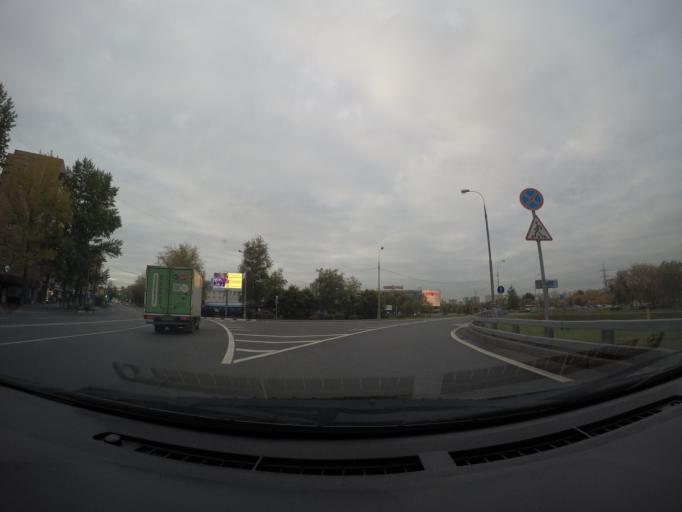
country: RU
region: Moscow
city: Ivanovskoye
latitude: 55.7687
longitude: 37.8457
